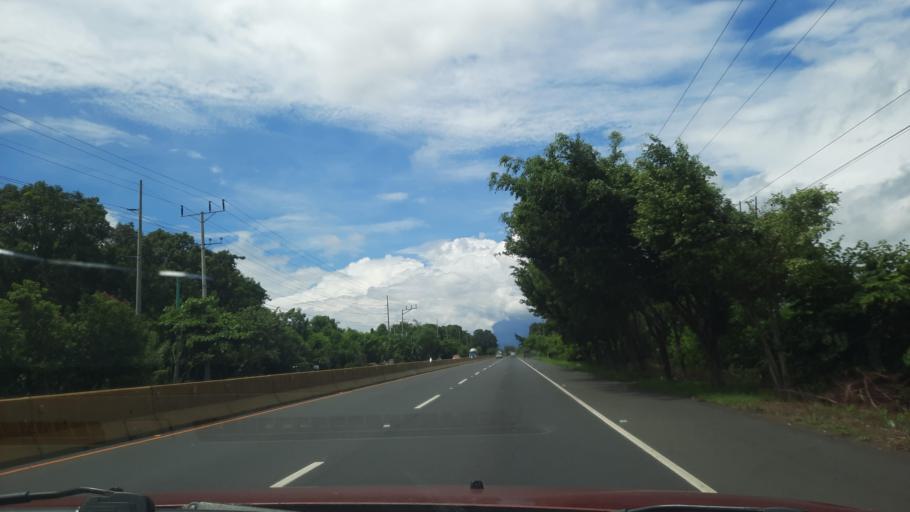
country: SV
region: Sonsonate
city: Acajutla
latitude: 13.6368
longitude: -89.7787
